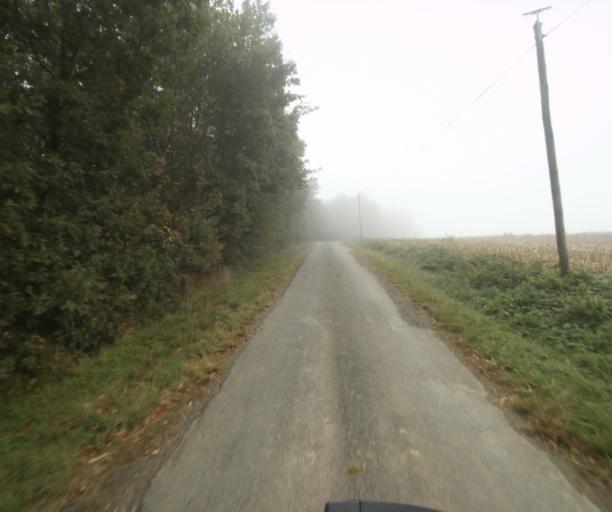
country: FR
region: Midi-Pyrenees
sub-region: Departement du Tarn-et-Garonne
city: Nohic
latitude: 43.9090
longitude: 1.4725
